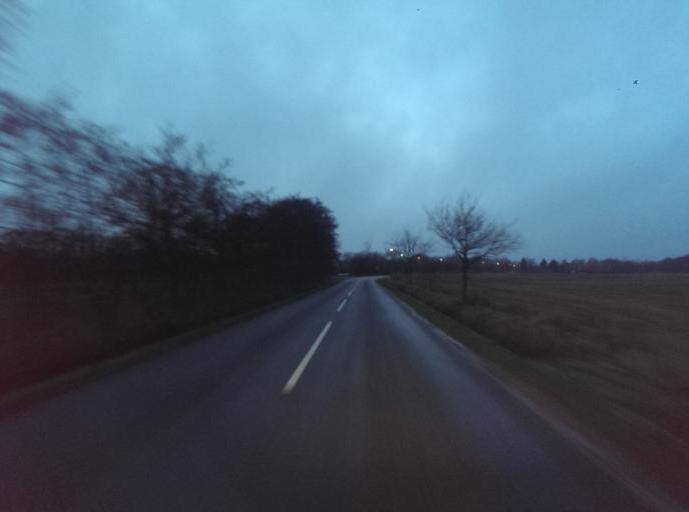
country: DK
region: South Denmark
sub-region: Esbjerg Kommune
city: Tjaereborg
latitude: 55.4924
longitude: 8.5409
